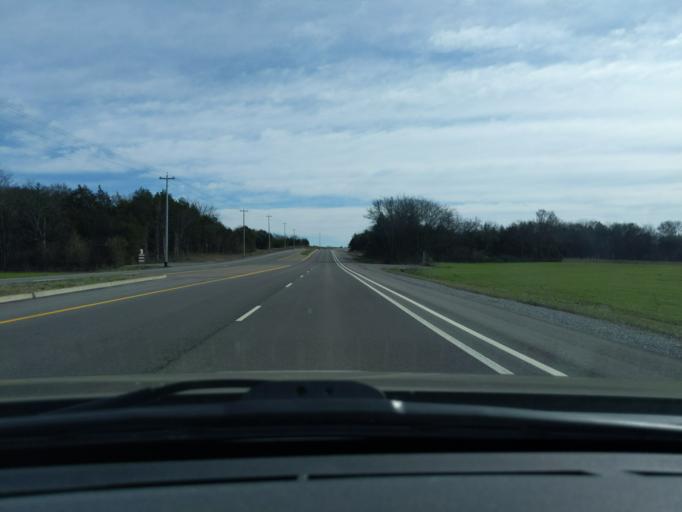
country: US
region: Tennessee
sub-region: Wilson County
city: Mount Juliet
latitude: 36.1986
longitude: -86.4863
